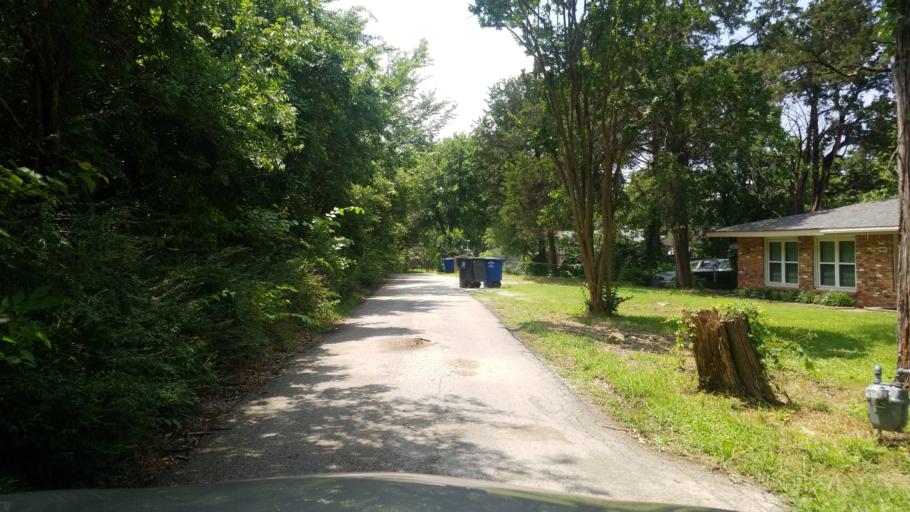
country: US
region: Texas
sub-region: Dallas County
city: Duncanville
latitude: 32.6810
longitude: -96.9245
